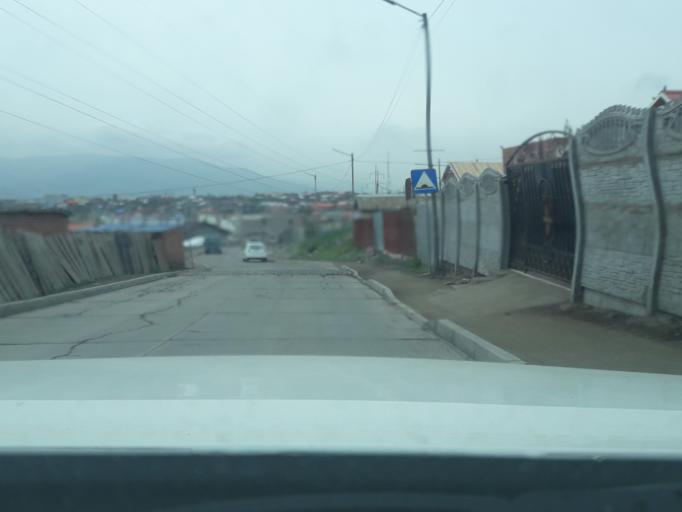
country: MN
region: Ulaanbaatar
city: Ulaanbaatar
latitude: 47.9486
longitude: 106.9044
